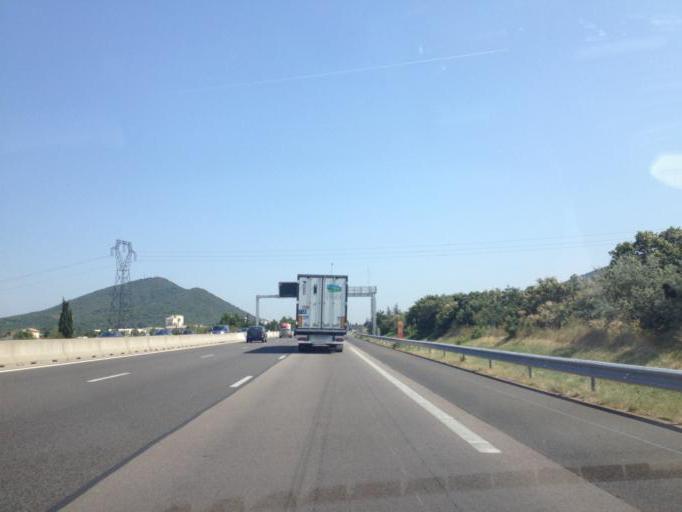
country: FR
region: Rhone-Alpes
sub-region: Departement de la Drome
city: Malataverne
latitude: 44.4546
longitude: 4.7564
